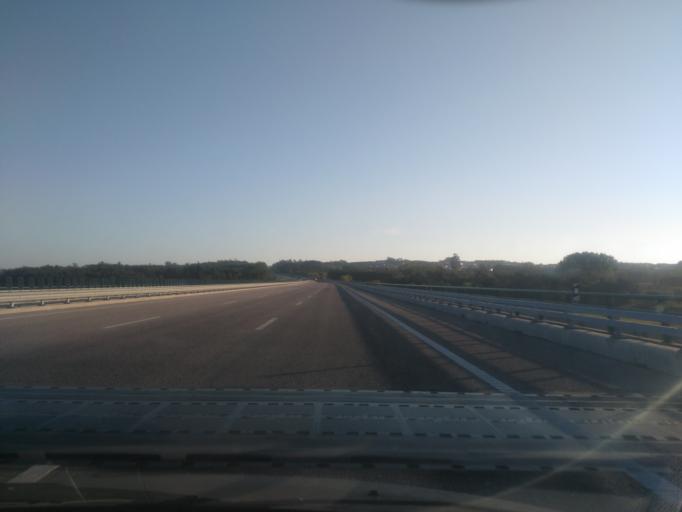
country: PT
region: Coimbra
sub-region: Figueira da Foz
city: Lavos
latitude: 40.0940
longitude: -8.7581
